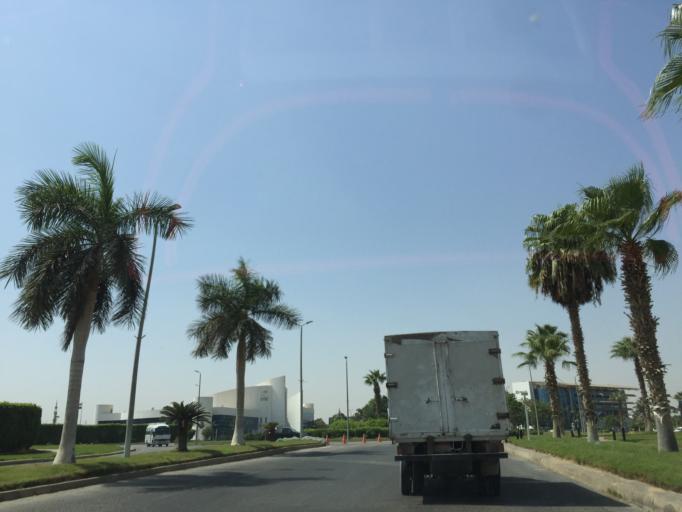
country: EG
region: Al Jizah
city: Awsim
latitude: 30.0694
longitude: 31.0189
